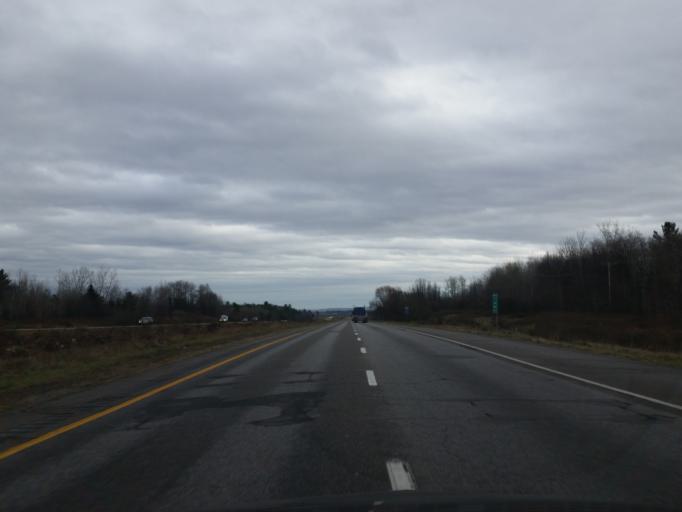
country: CA
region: Quebec
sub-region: Outaouais
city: Gatineau
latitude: 45.5111
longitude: -75.6361
